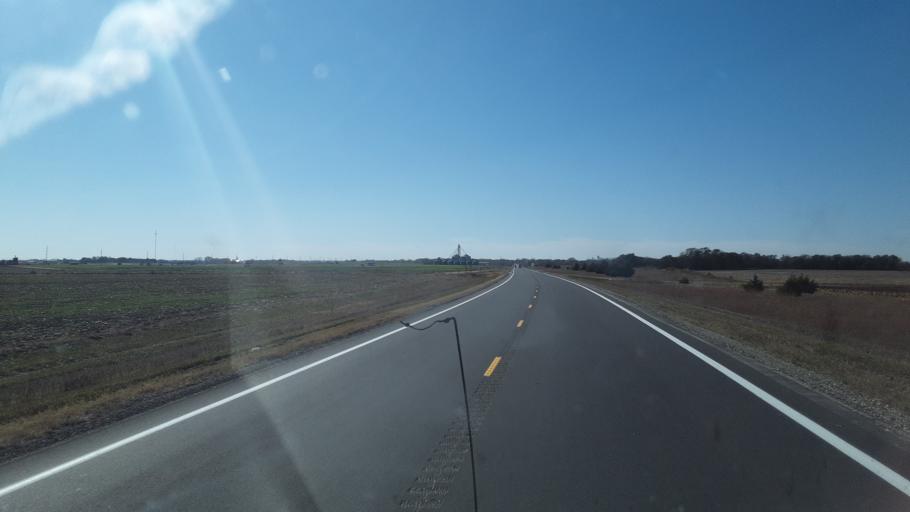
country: US
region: Kansas
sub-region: Rice County
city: Lyons
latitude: 38.3637
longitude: -98.1624
